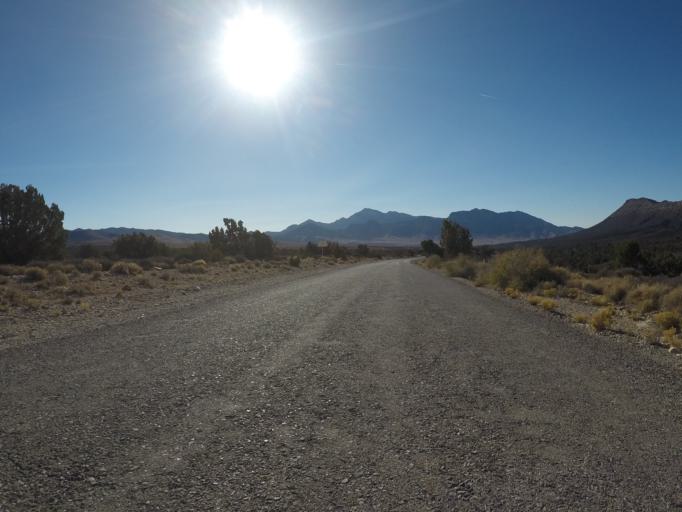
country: US
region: Nevada
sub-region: Clark County
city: Summerlin South
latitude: 36.0726
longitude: -115.5628
